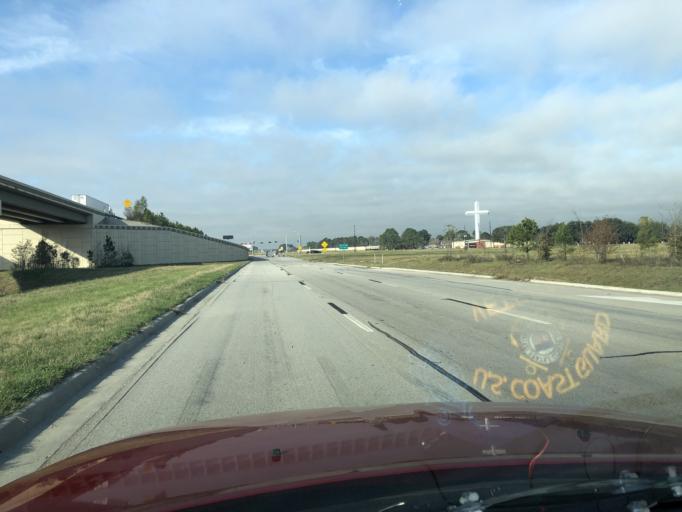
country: US
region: Texas
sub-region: Harris County
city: Tomball
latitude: 30.0522
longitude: -95.6176
